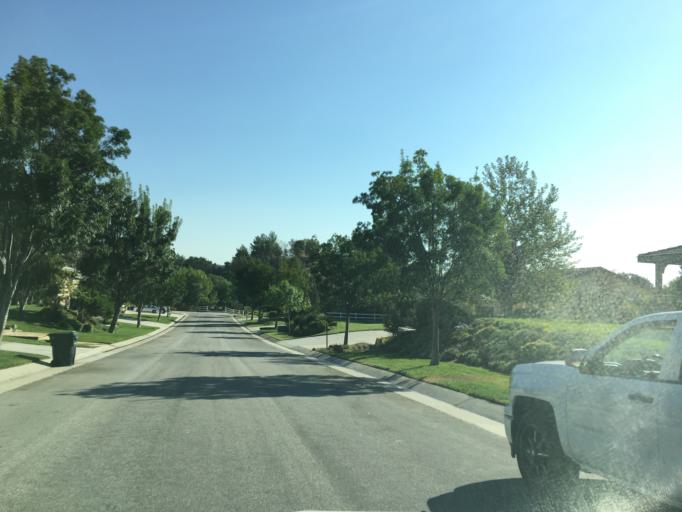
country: US
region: California
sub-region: Los Angeles County
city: Val Verde
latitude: 34.4653
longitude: -118.6661
